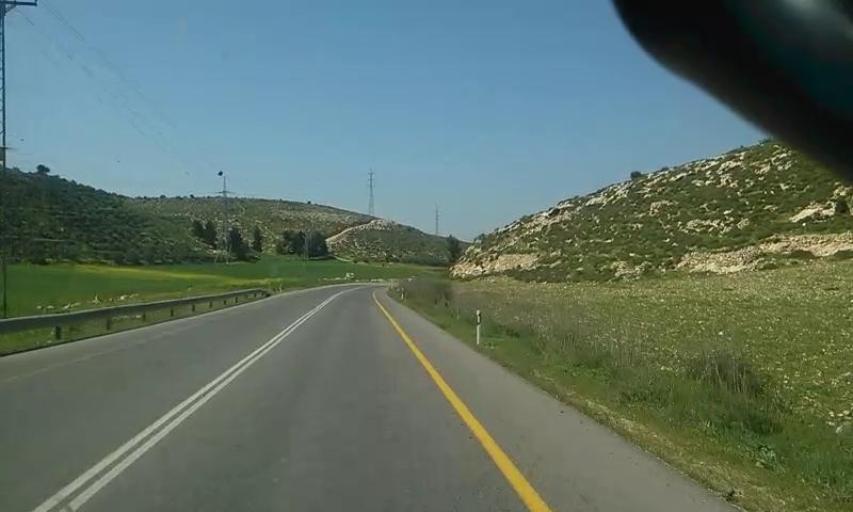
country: PS
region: West Bank
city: Idhna
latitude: 31.5820
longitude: 34.9744
